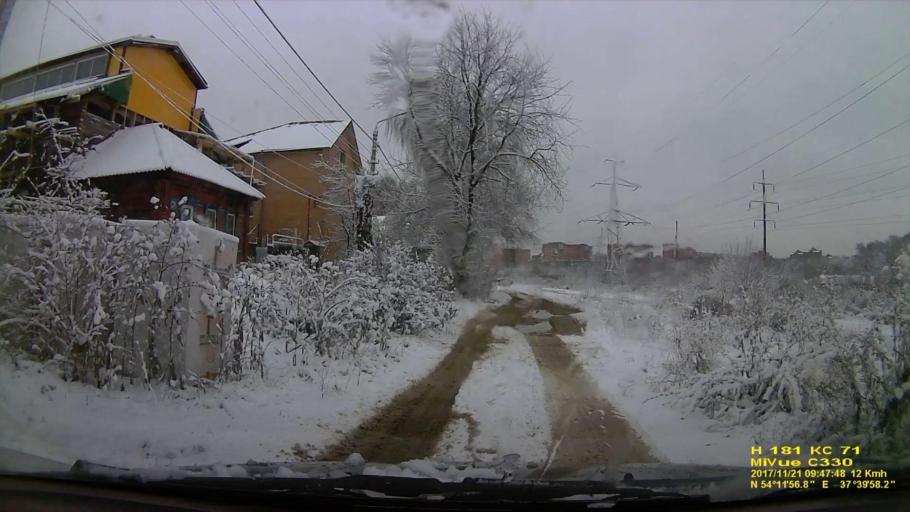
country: RU
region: Tula
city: Tula
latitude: 54.1992
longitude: 37.6665
